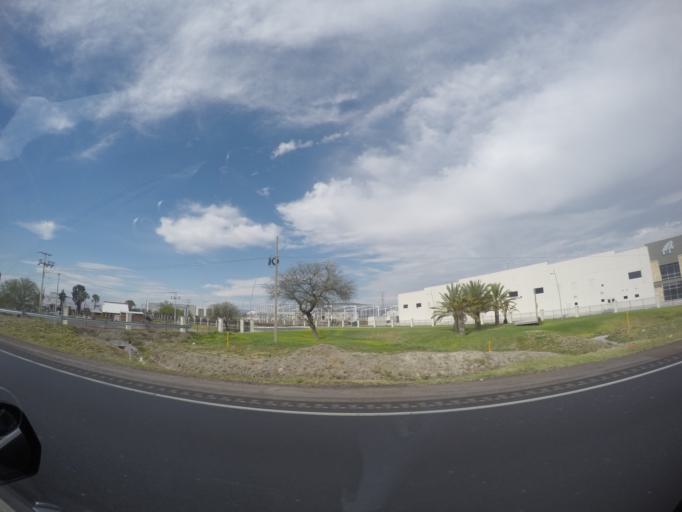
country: MX
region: Guanajuato
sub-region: Apaseo el Grande
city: La Labor
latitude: 20.5372
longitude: -100.7239
